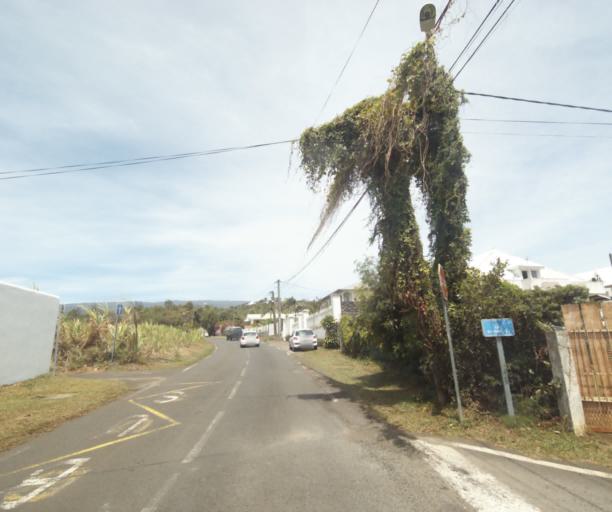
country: RE
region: Reunion
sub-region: Reunion
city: Saint-Paul
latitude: -21.0484
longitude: 55.2744
